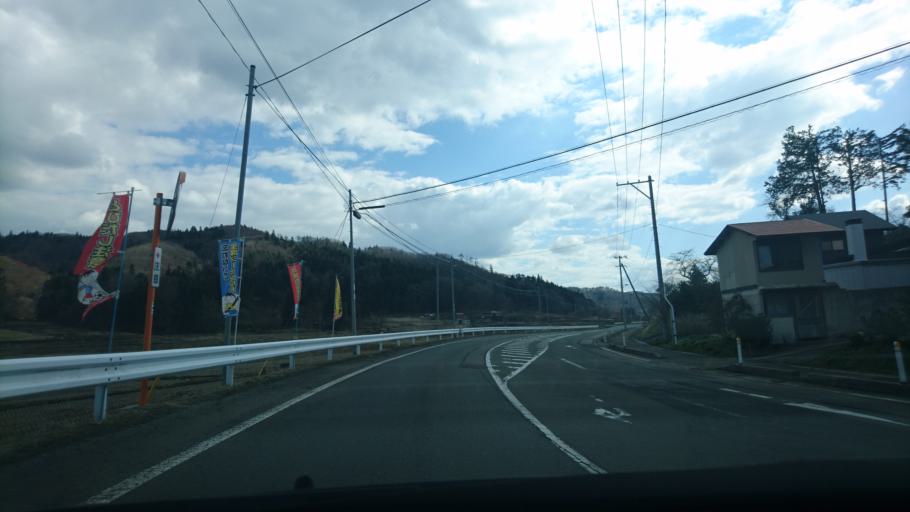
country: JP
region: Iwate
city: Hanamaki
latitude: 39.3352
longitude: 141.2393
